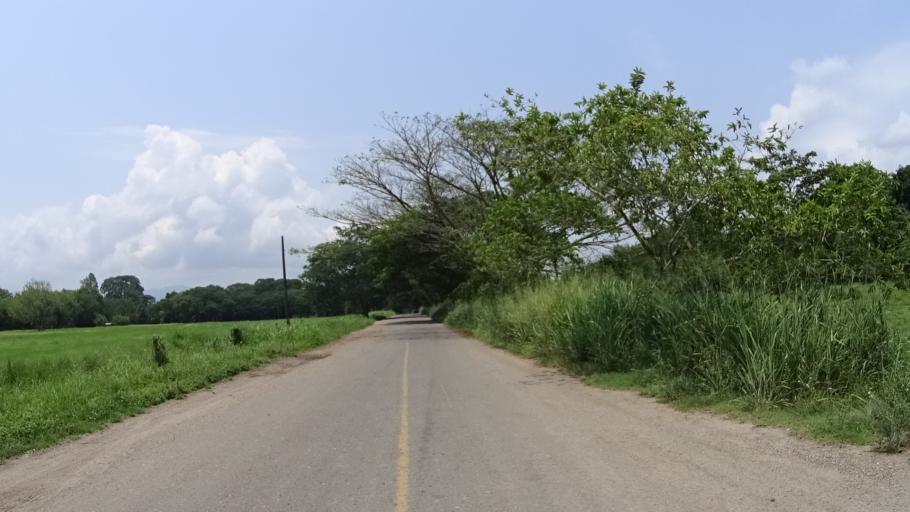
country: CO
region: Cundinamarca
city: Puerto Salgar
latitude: 5.5041
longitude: -74.6887
